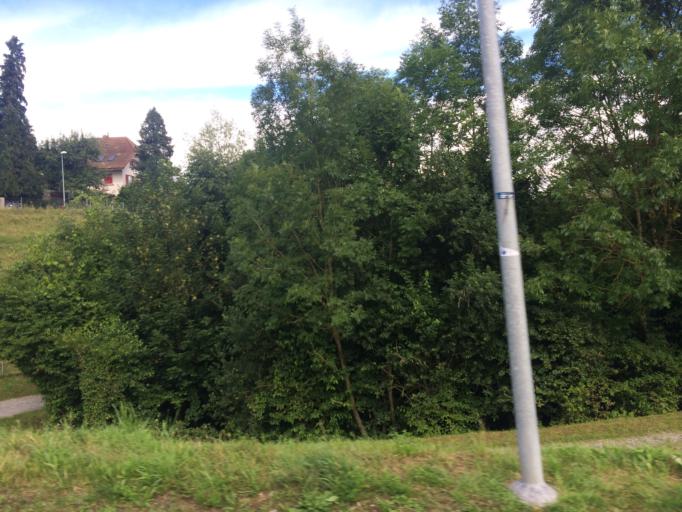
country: CH
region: Bern
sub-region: Bern-Mittelland District
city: Zollikofen
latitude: 46.9824
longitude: 7.4575
